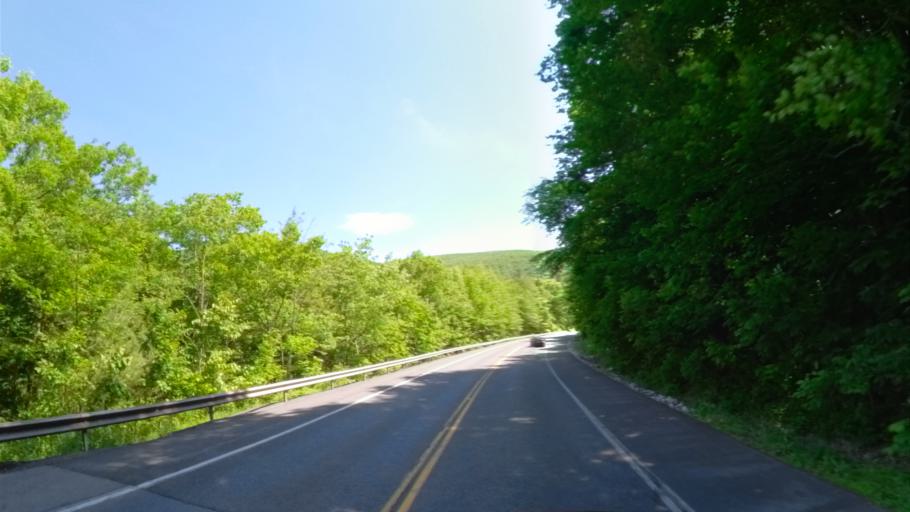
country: US
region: New York
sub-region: Ulster County
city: Shokan
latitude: 42.1137
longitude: -74.4277
